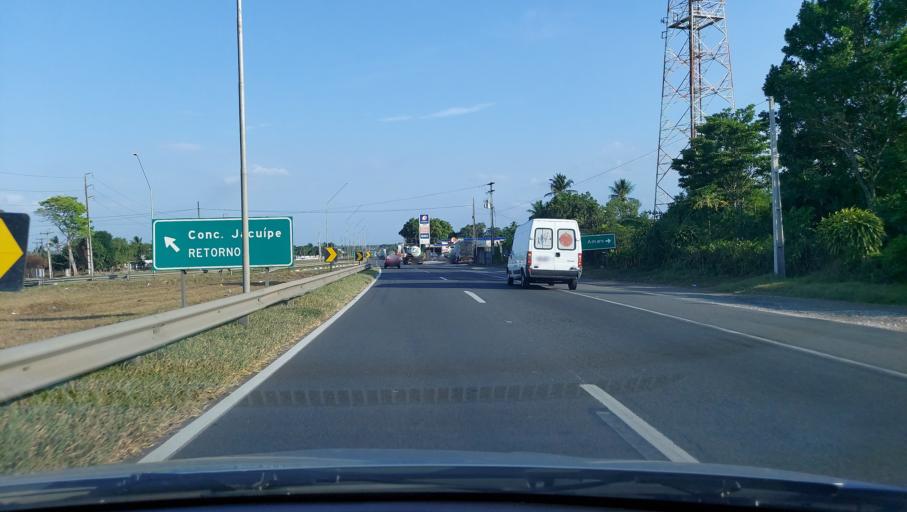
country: BR
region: Bahia
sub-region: Conceicao Do Jacuipe
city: Conceicao do Jacuipe
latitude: -12.3765
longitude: -38.8040
